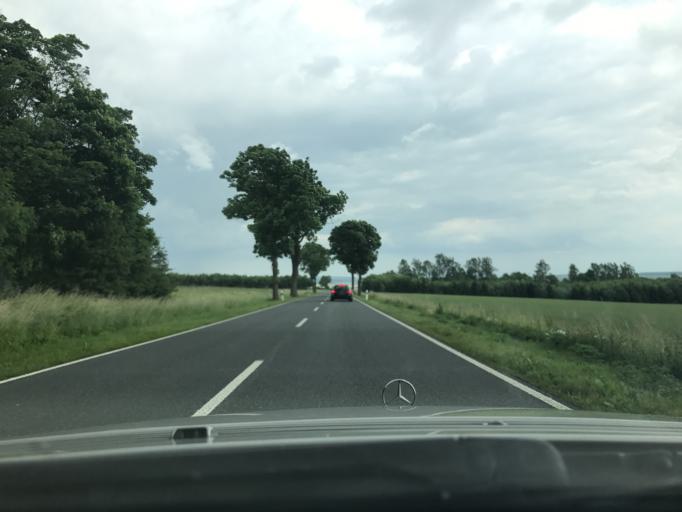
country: DE
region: Thuringia
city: Kefferhausen
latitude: 51.3350
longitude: 10.2787
